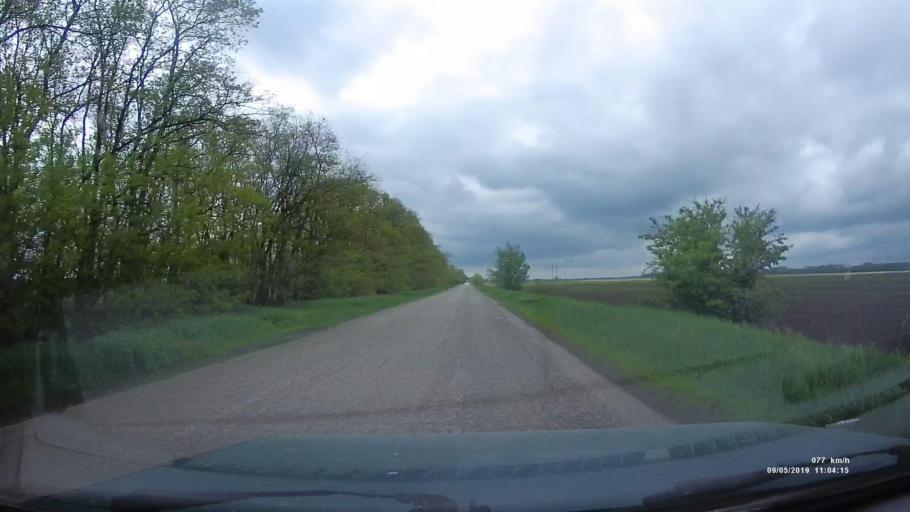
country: RU
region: Krasnodarskiy
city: Kanelovskaya
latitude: 46.8193
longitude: 39.2100
